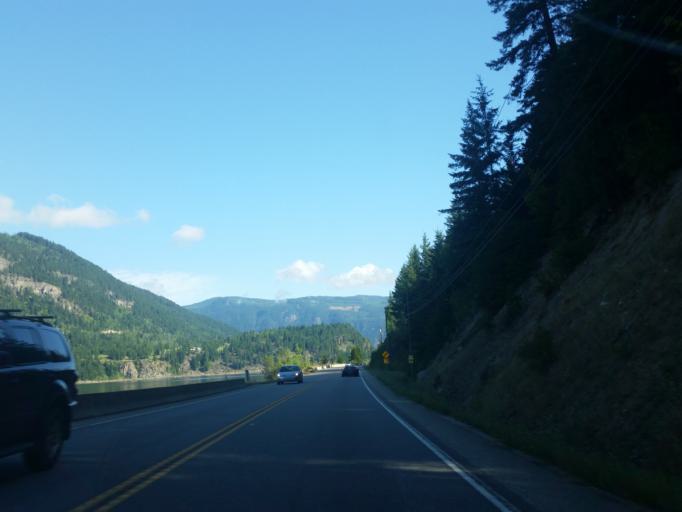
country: CA
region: British Columbia
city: Sicamous
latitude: 50.7855
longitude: -118.9946
